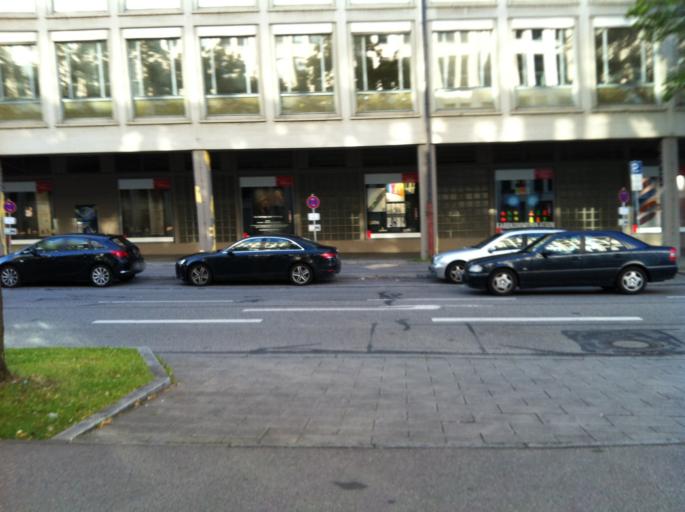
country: DE
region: Bavaria
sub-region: Upper Bavaria
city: Munich
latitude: 48.1437
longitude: 11.5633
